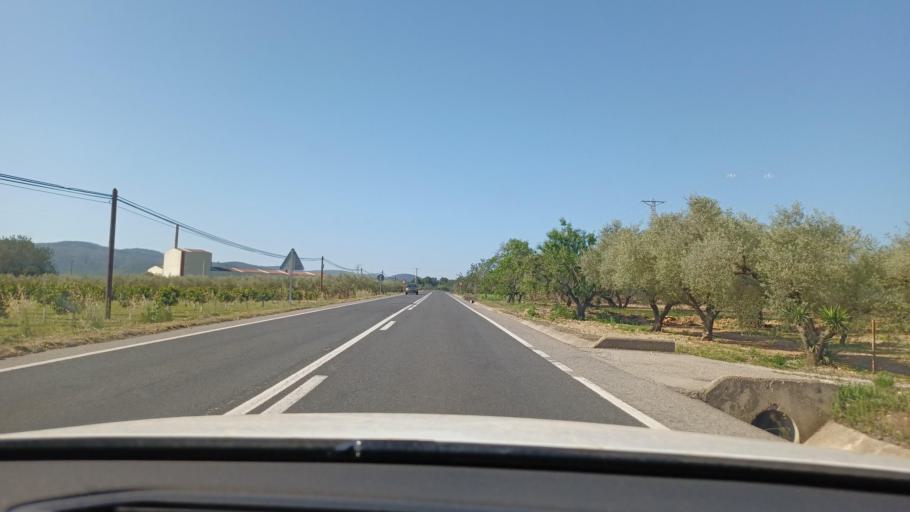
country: ES
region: Catalonia
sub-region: Provincia de Tarragona
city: Santa Barbara
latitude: 40.7044
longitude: 0.4822
